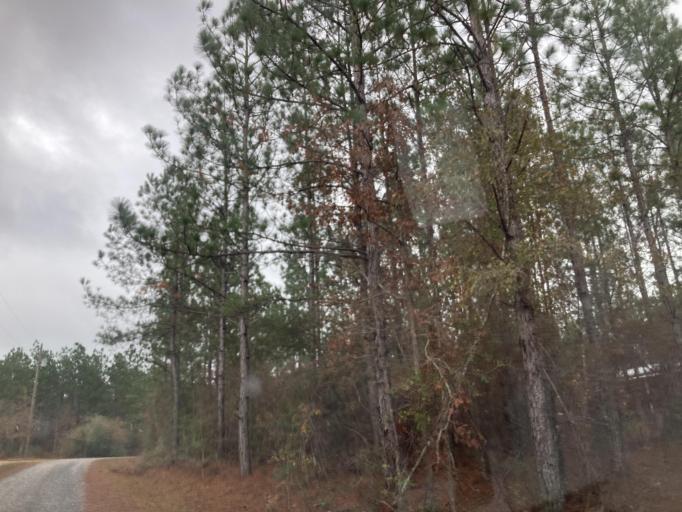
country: US
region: Mississippi
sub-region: Lamar County
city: Lumberton
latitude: 31.1064
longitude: -89.5928
